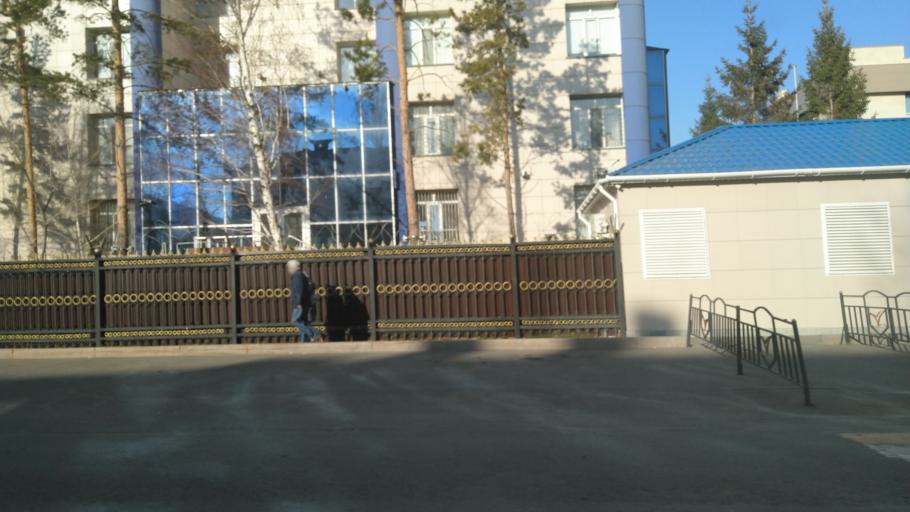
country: KZ
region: Pavlodar
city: Pavlodar
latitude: 52.2906
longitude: 76.9456
